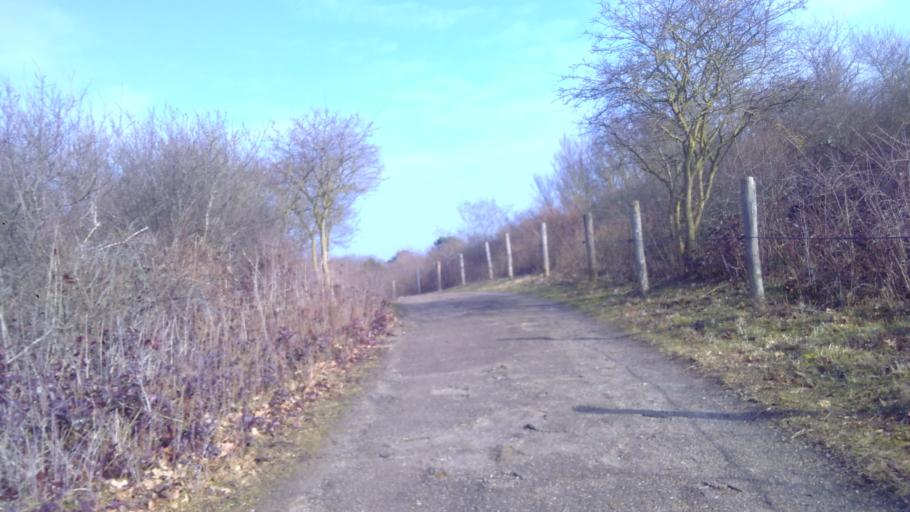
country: NL
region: South Holland
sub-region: Gemeente Den Haag
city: Scheveningen
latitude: 52.0842
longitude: 4.2539
